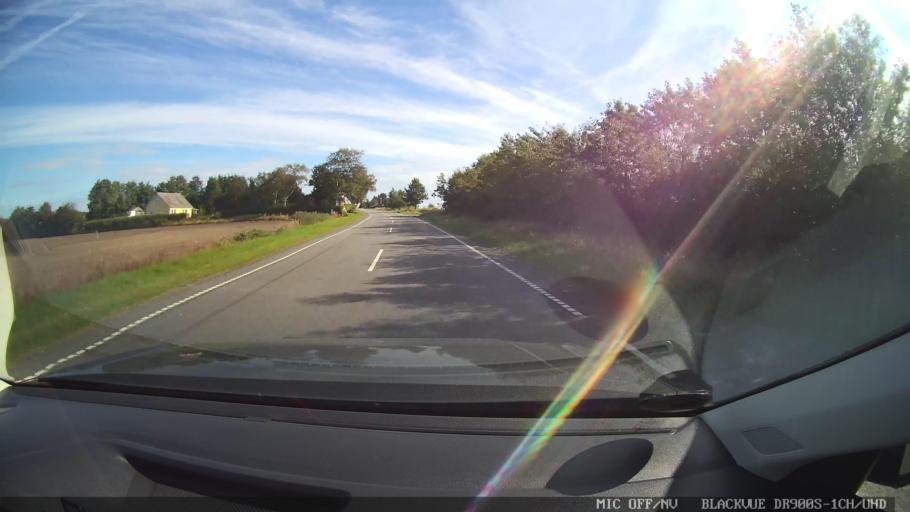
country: DK
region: North Denmark
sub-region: Rebild Kommune
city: Skorping
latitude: 56.7719
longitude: 9.9969
